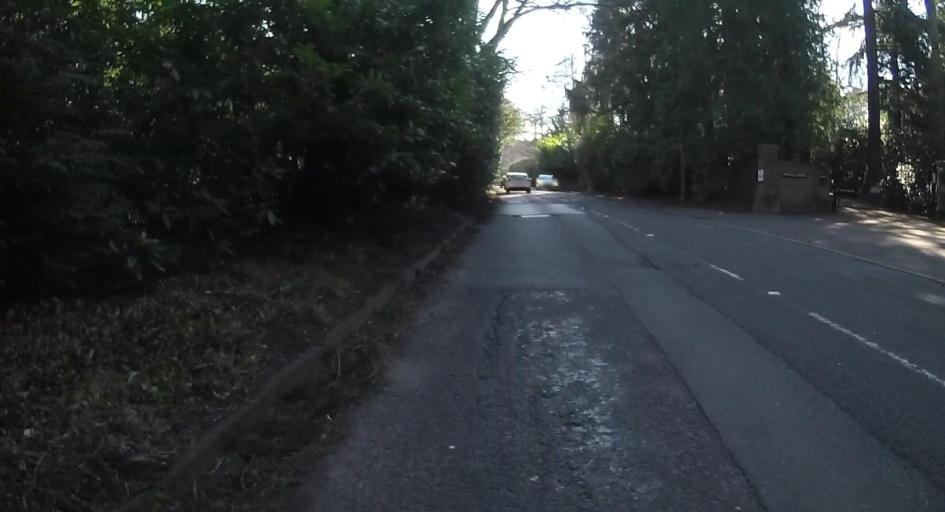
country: GB
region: England
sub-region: Surrey
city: Windlesham
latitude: 51.3813
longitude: -0.6725
